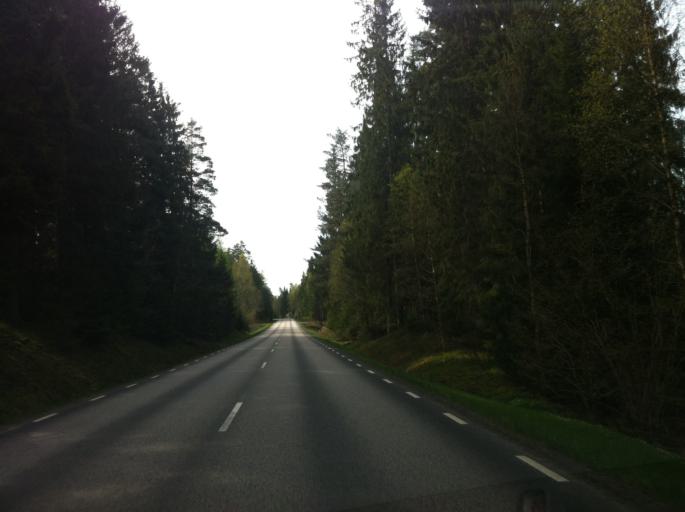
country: SE
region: Vaestra Goetaland
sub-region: Marks Kommun
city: Kinna
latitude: 57.4117
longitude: 12.7740
